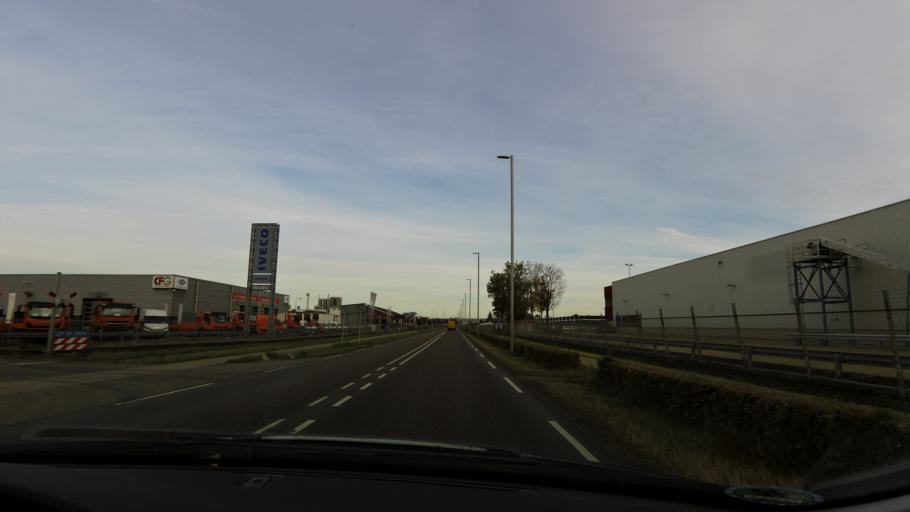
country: NL
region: Limburg
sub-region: Gemeente Sittard-Geleen
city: Born
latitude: 51.0500
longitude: 5.8160
